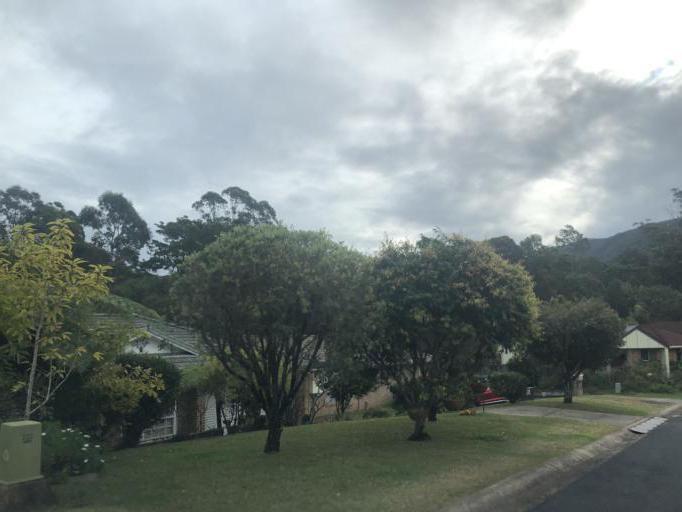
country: AU
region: New South Wales
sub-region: Coffs Harbour
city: Coffs Harbour
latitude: -30.2777
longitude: 153.1099
